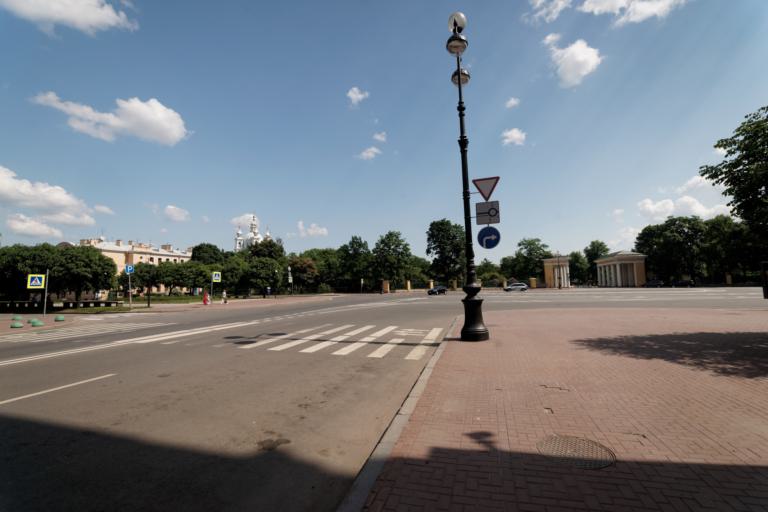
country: RU
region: St.-Petersburg
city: Centralniy
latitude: 59.9467
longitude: 30.3894
